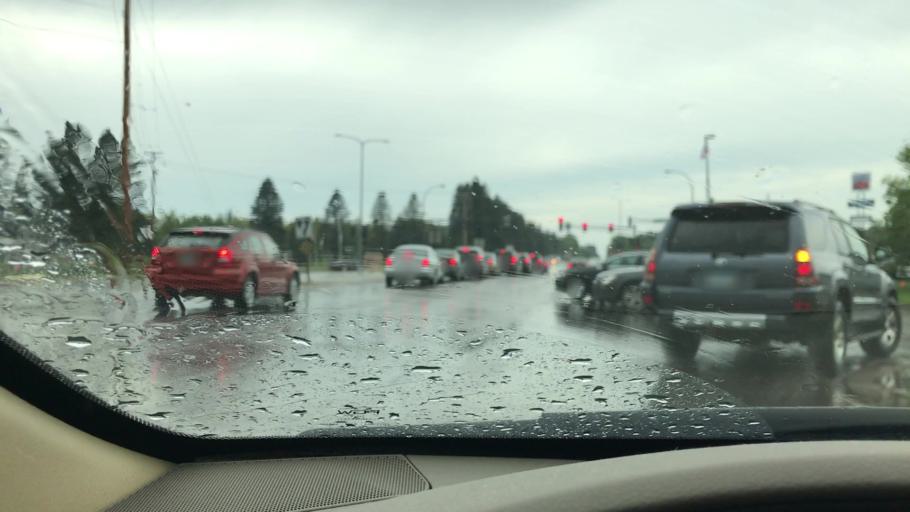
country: US
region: Minnesota
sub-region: Saint Louis County
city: Hermantown
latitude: 46.8222
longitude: -92.1853
